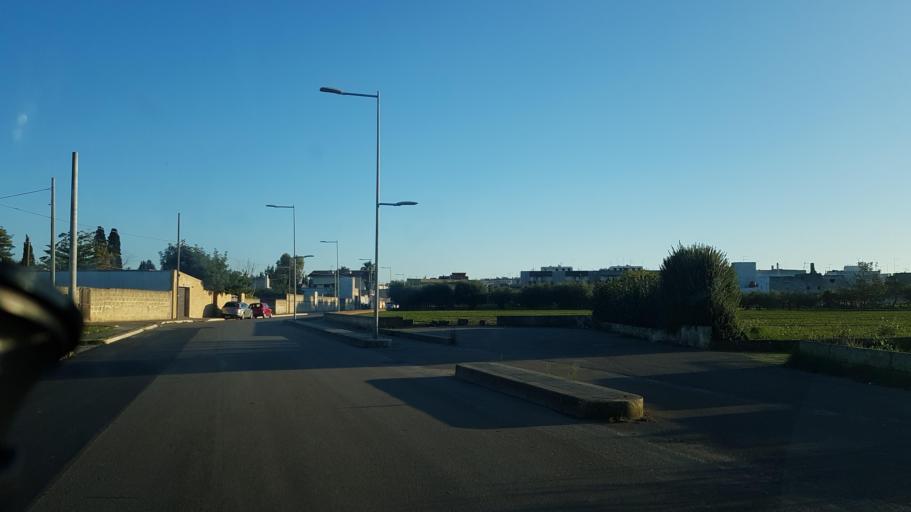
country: IT
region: Apulia
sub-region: Provincia di Brindisi
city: Latiano
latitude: 40.5568
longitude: 17.7235
